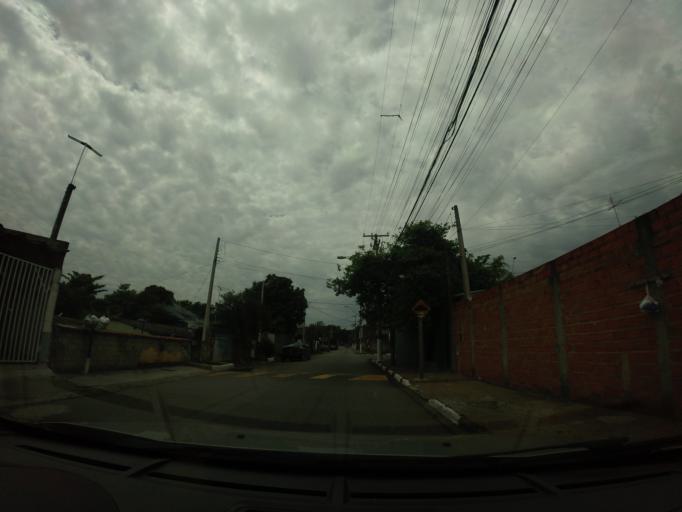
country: BR
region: Sao Paulo
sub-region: Hortolandia
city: Hortolandia
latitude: -22.8423
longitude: -47.1658
